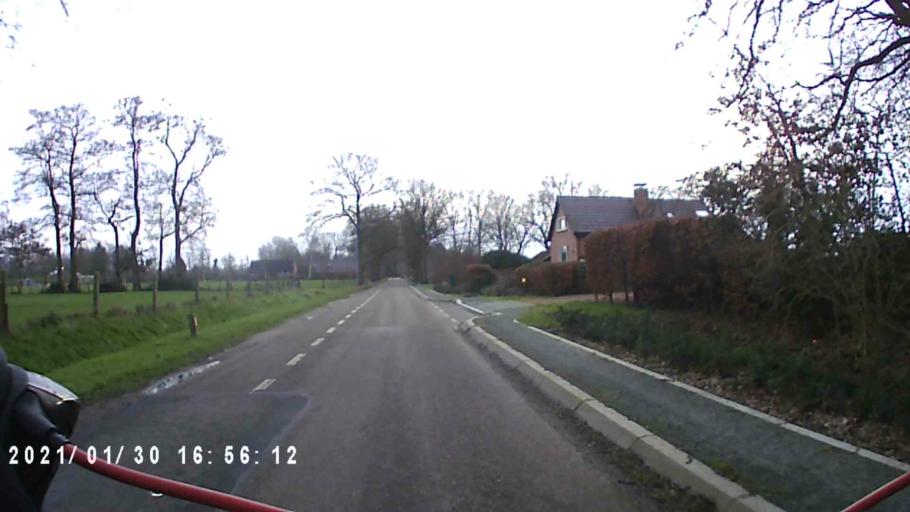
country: NL
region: Groningen
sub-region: Gemeente Leek
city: Leek
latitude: 53.1515
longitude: 6.3817
